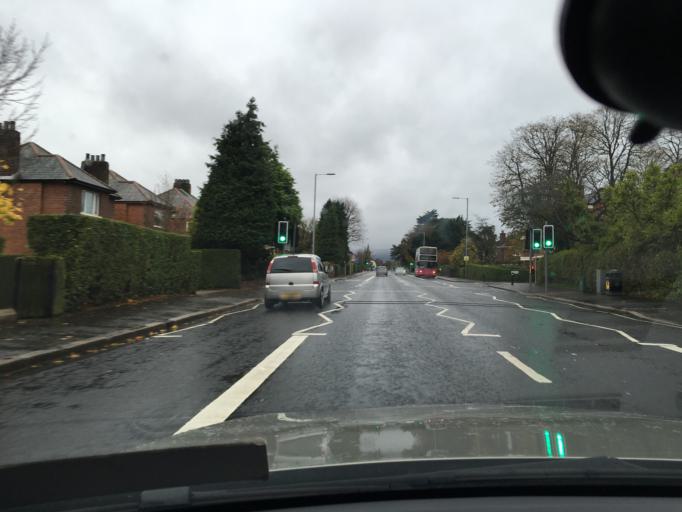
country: GB
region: Northern Ireland
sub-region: Castlereagh District
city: Castlereagh
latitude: 54.5948
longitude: -5.8581
